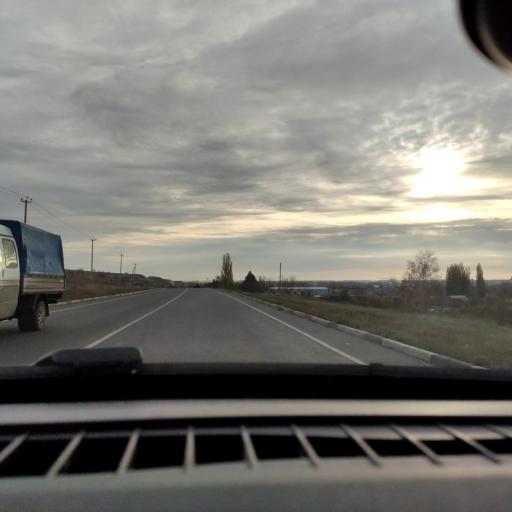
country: RU
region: Belgorod
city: Alekseyevka
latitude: 50.6431
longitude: 38.6488
